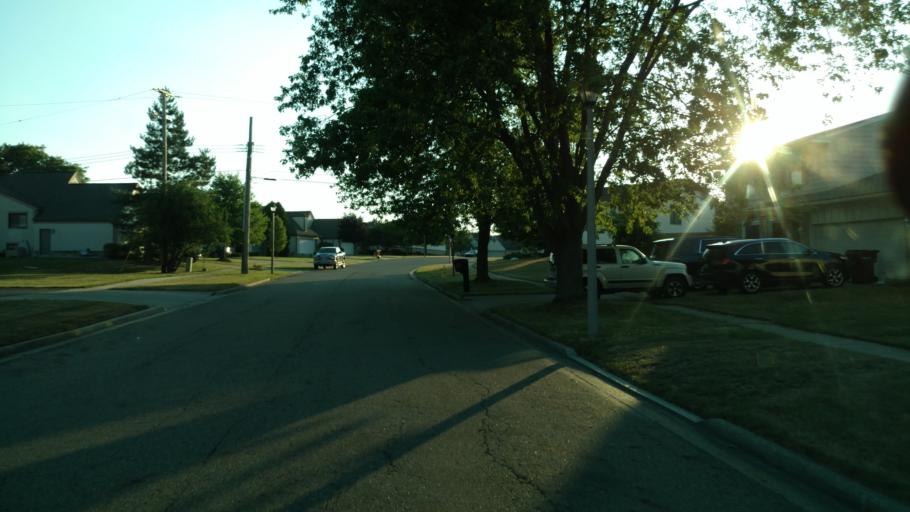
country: US
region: Michigan
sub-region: Eaton County
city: Waverly
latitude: 42.7211
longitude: -84.6173
